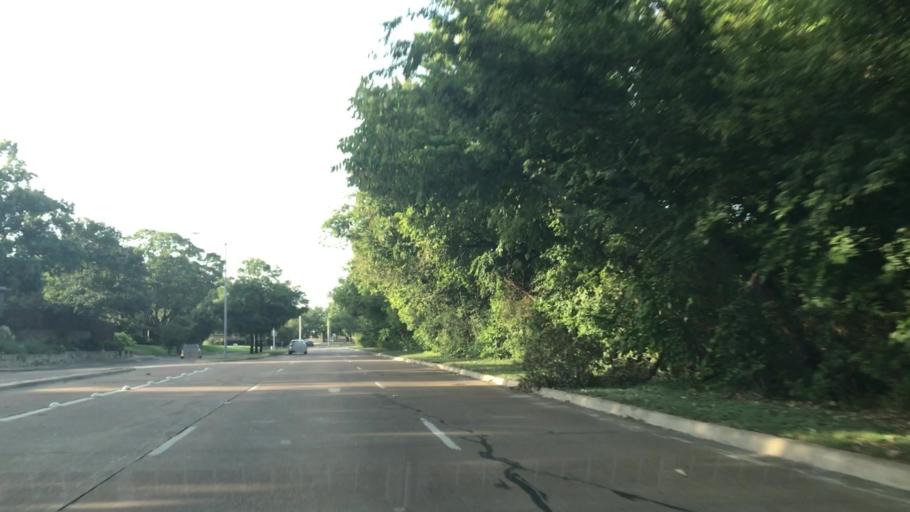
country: US
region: Texas
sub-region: Dallas County
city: Garland
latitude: 32.8492
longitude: -96.7030
